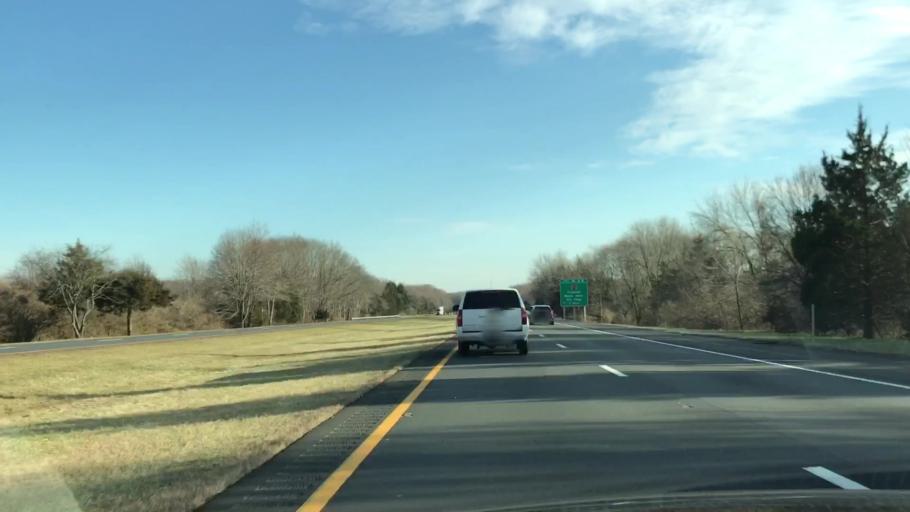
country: US
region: New Jersey
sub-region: Monmouth County
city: Shrewsbury
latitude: 40.1692
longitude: -74.4444
